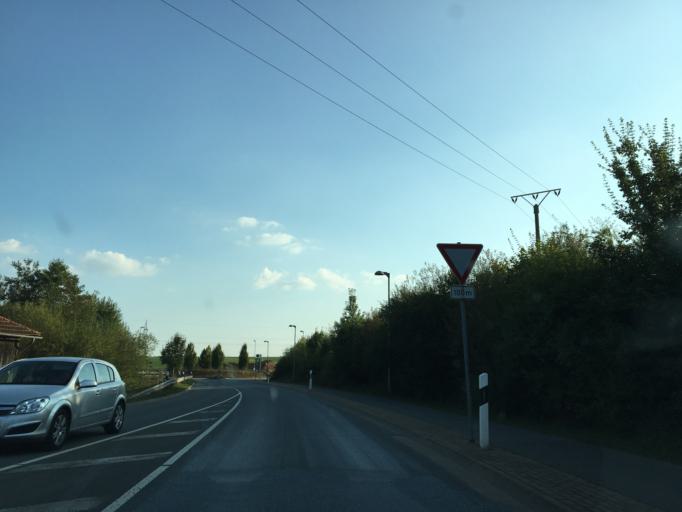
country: DE
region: Hesse
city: Frankenberg
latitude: 51.0498
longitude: 8.8025
